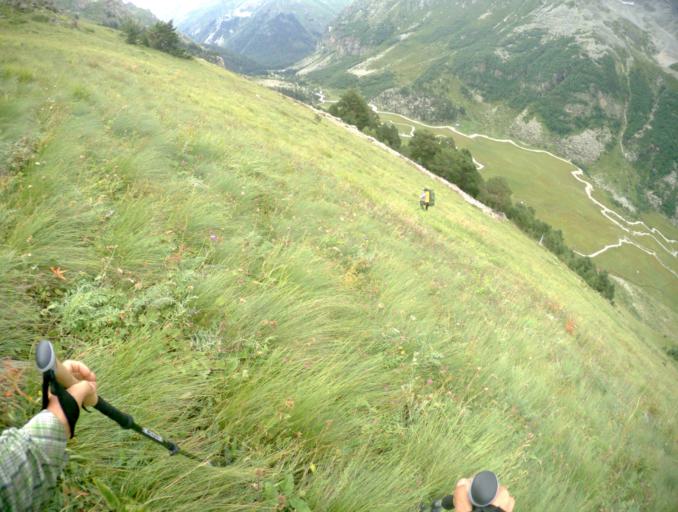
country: RU
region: Karachayevo-Cherkesiya
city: Uchkulan
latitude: 43.2689
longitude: 42.1353
